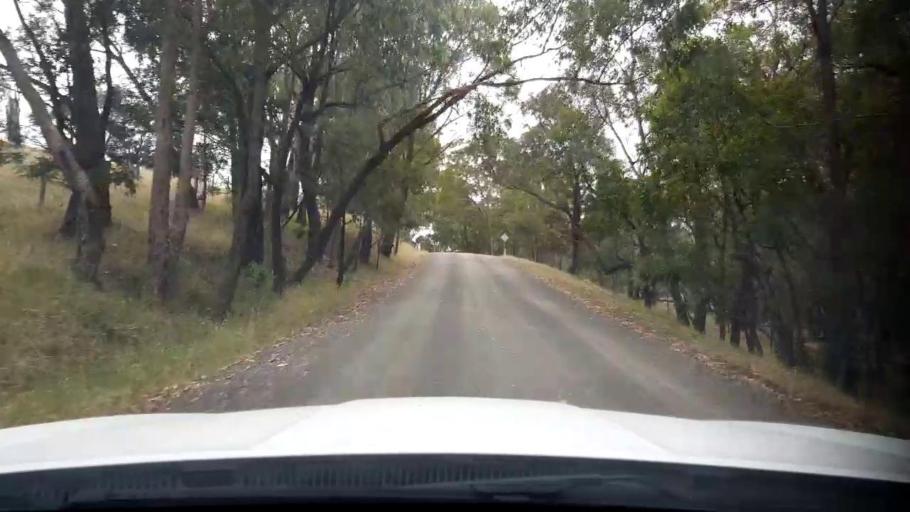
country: AU
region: Victoria
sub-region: Whittlesea
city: Whittlesea
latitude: -37.4841
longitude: 145.0594
